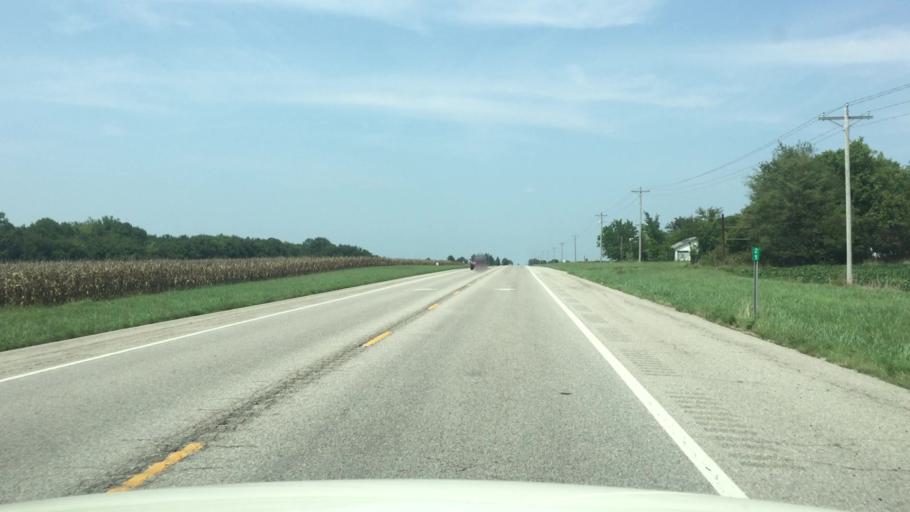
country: US
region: Kansas
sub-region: Crawford County
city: Pittsburg
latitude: 37.2603
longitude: -94.7052
